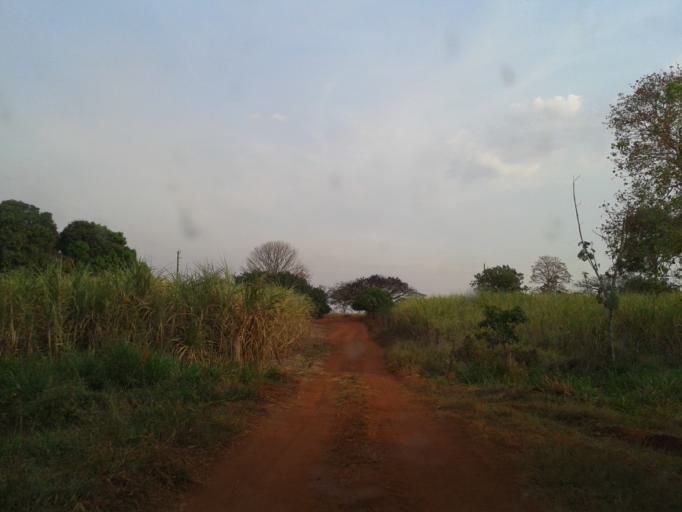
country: BR
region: Minas Gerais
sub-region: Capinopolis
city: Capinopolis
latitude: -18.8109
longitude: -49.7271
